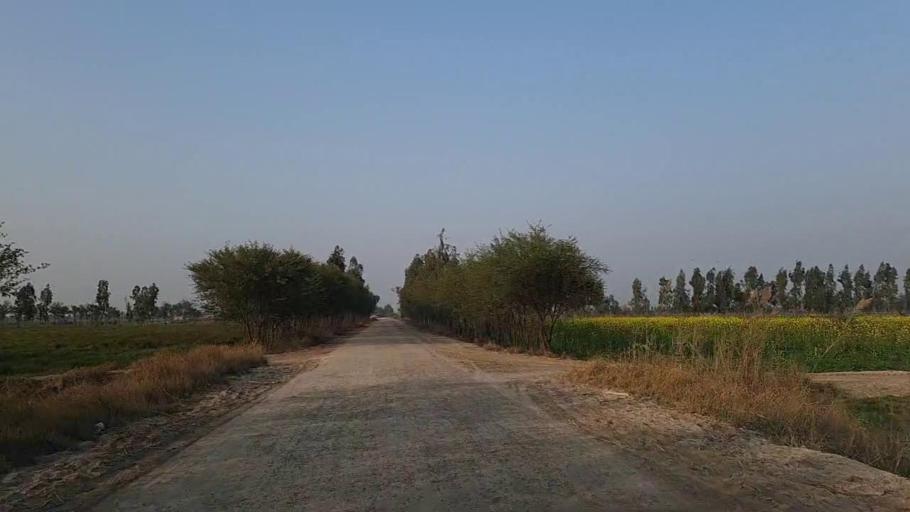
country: PK
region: Sindh
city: Daur
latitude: 26.4205
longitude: 68.3935
